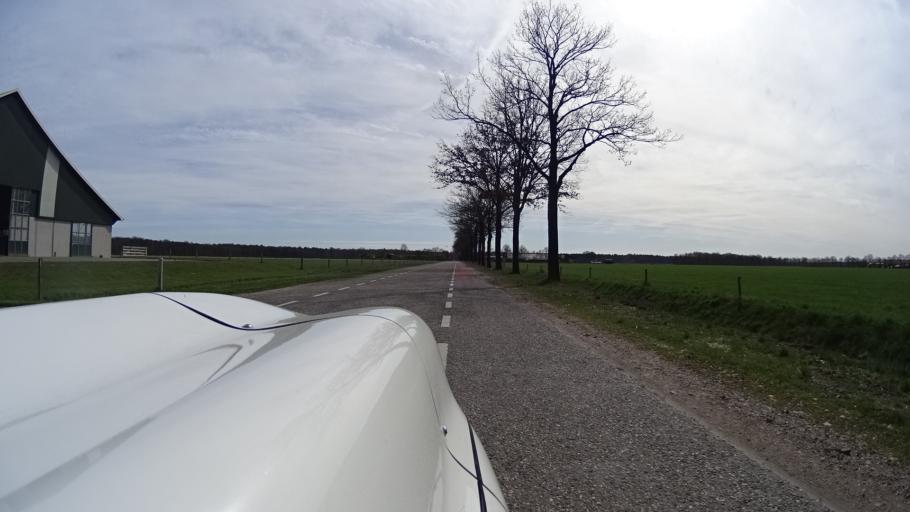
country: NL
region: Limburg
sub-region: Gemeente Venlo
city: Arcen
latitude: 51.5206
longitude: 6.2005
